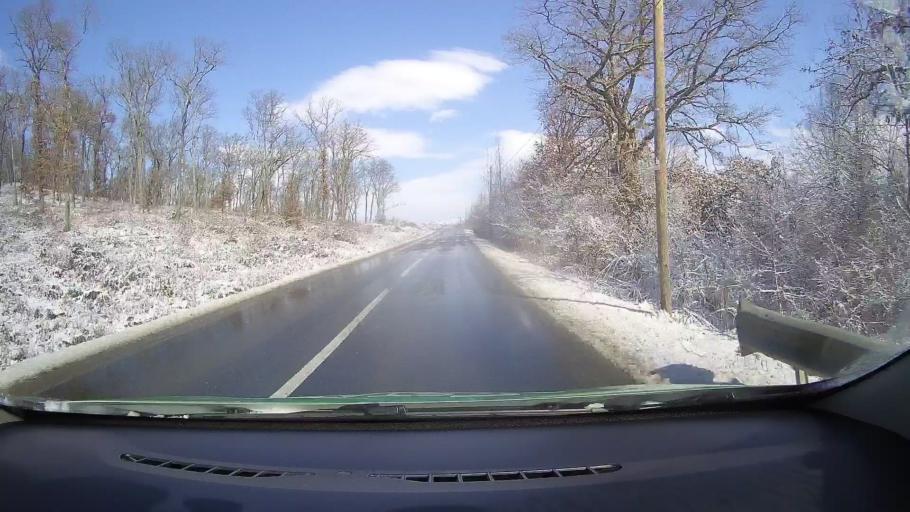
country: RO
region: Sibiu
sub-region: Comuna Nocrich
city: Nocrich
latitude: 45.8611
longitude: 24.4526
